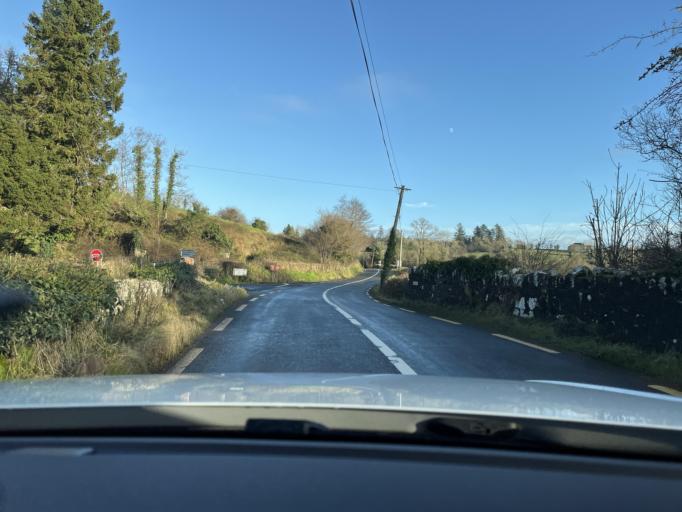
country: IE
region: Connaught
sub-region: County Leitrim
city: Manorhamilton
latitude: 54.1755
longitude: -8.1092
